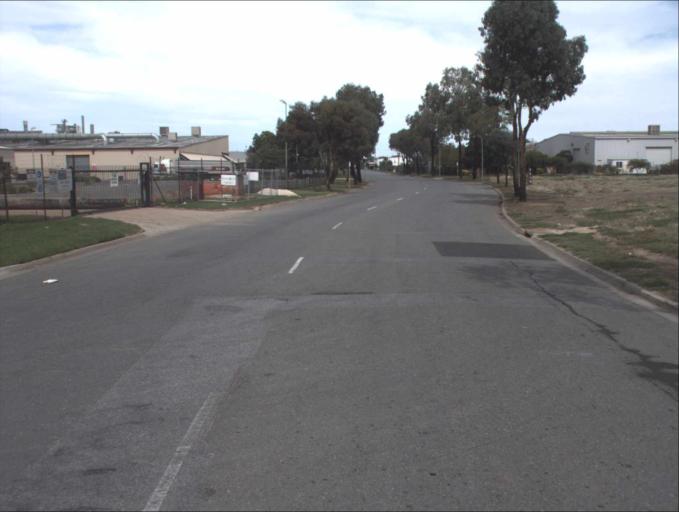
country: AU
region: South Australia
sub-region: Port Adelaide Enfield
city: Blair Athol
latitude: -34.8425
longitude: 138.5700
